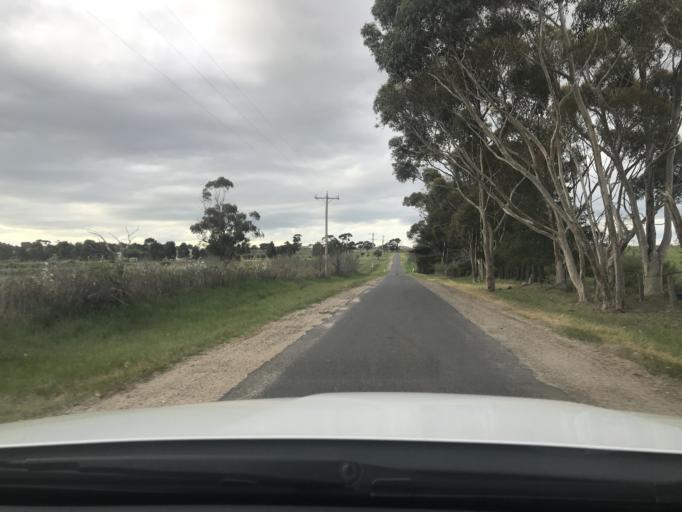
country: AU
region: Victoria
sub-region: Hume
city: Roxburgh Park
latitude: -37.5848
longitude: 144.8912
